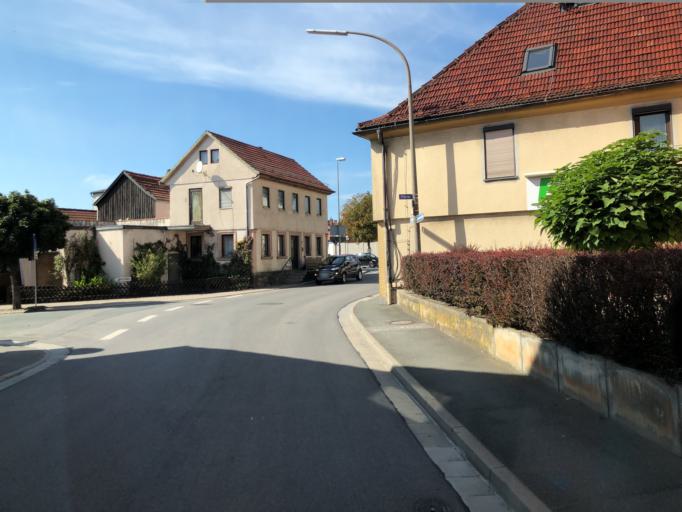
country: DE
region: Bavaria
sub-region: Upper Franconia
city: Michelau
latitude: 50.1618
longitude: 11.1124
